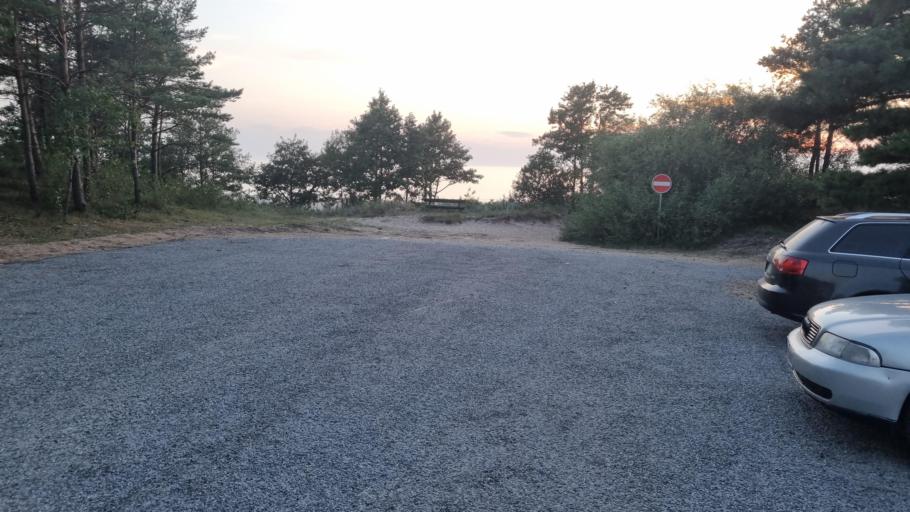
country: LV
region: Ventspils
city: Ventspils
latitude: 57.2469
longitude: 21.4148
